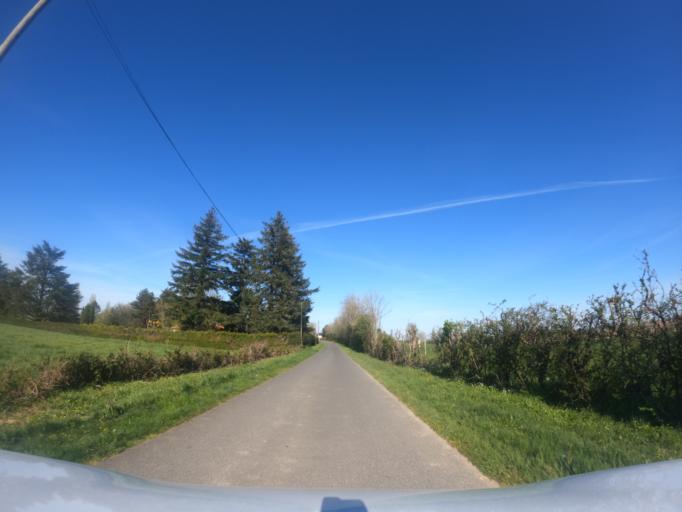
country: FR
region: Pays de la Loire
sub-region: Departement de la Vendee
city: Saint-Pierre-du-Chemin
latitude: 46.6891
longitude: -0.7022
